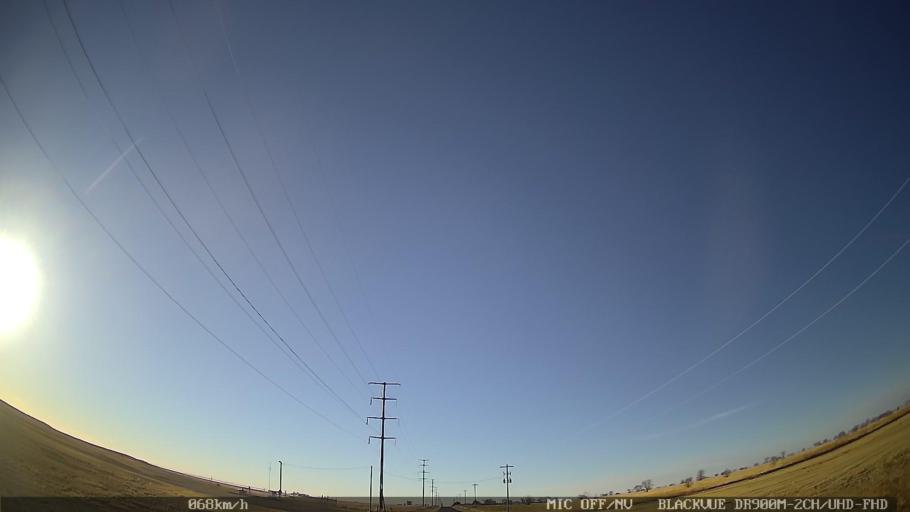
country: US
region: New Mexico
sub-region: Curry County
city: Clovis
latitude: 34.4314
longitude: -103.2493
